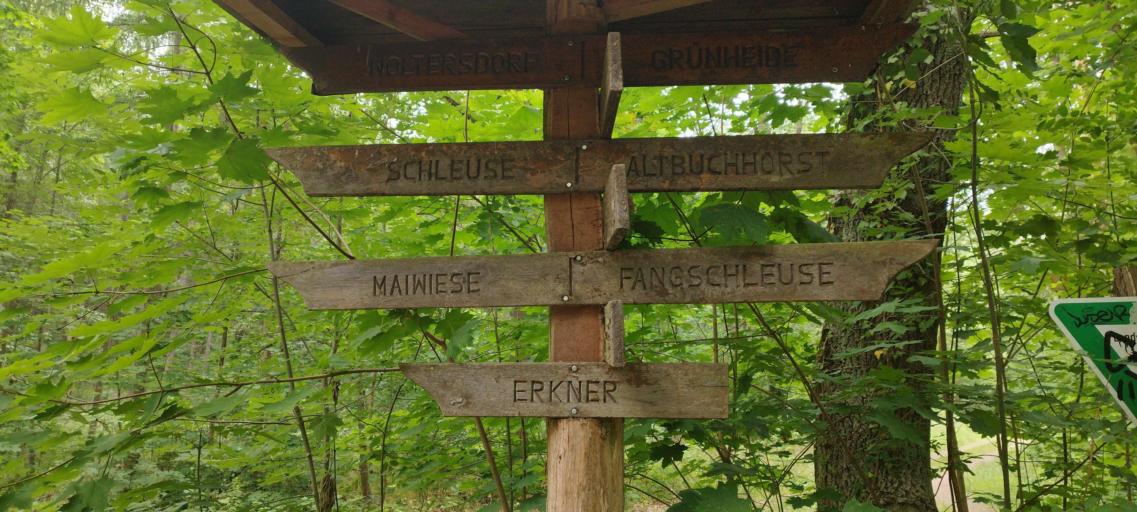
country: DE
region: Brandenburg
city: Woltersdorf
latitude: 52.4394
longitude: 13.7803
